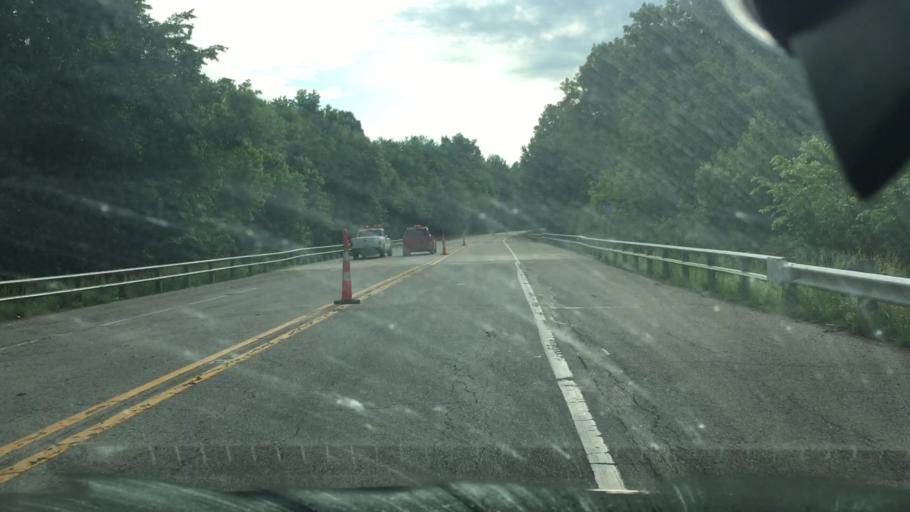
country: US
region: Kentucky
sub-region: Hancock County
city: Lewisport
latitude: 37.9501
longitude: -86.9624
